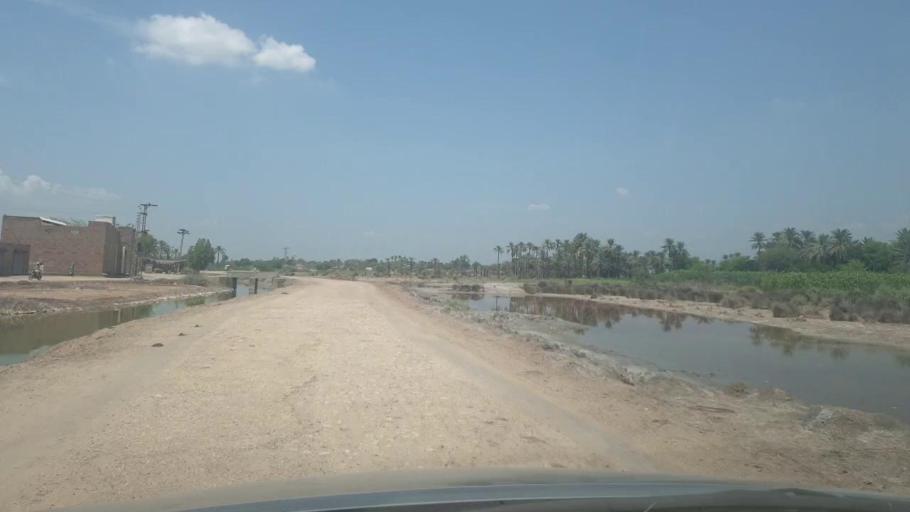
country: PK
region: Sindh
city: Kot Diji
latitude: 27.4146
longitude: 68.7370
